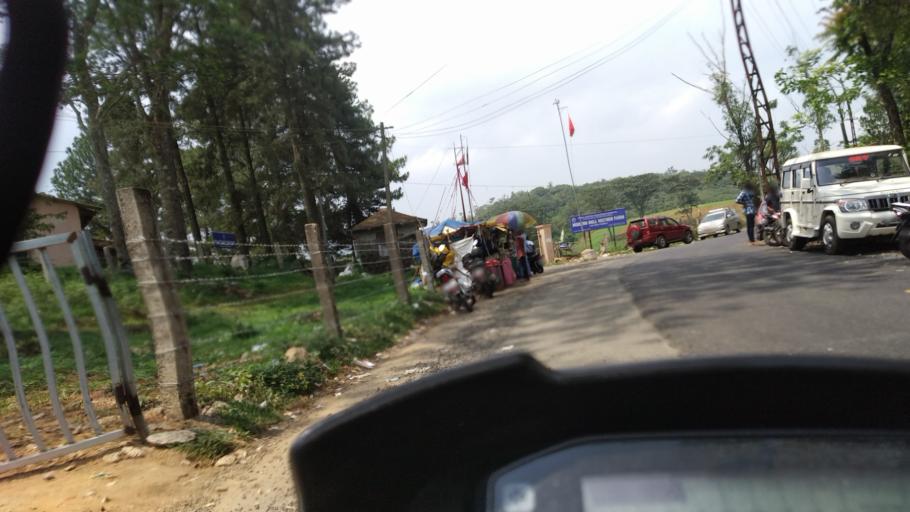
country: IN
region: Kerala
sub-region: Kottayam
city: Erattupetta
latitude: 9.6532
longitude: 76.9276
